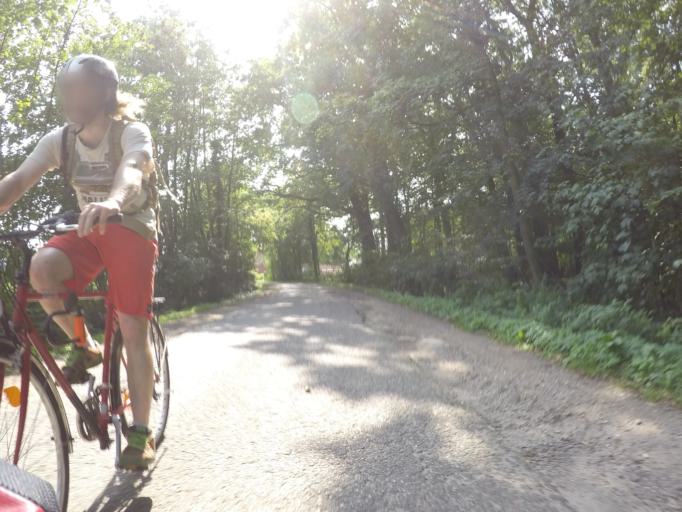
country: DE
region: Schleswig-Holstein
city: Kisdorf
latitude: 53.7955
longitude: 10.0308
